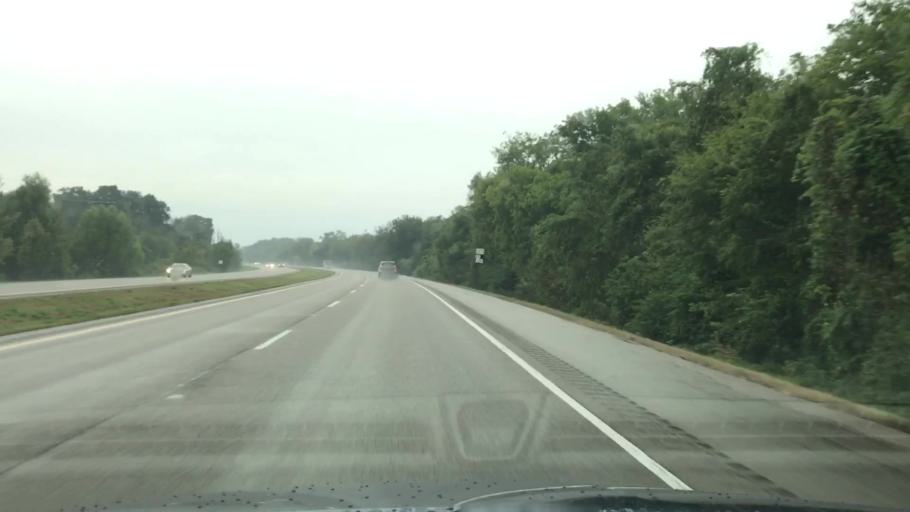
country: US
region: Louisiana
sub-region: Saint Charles Parish
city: Paradis
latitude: 29.8566
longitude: -90.4476
